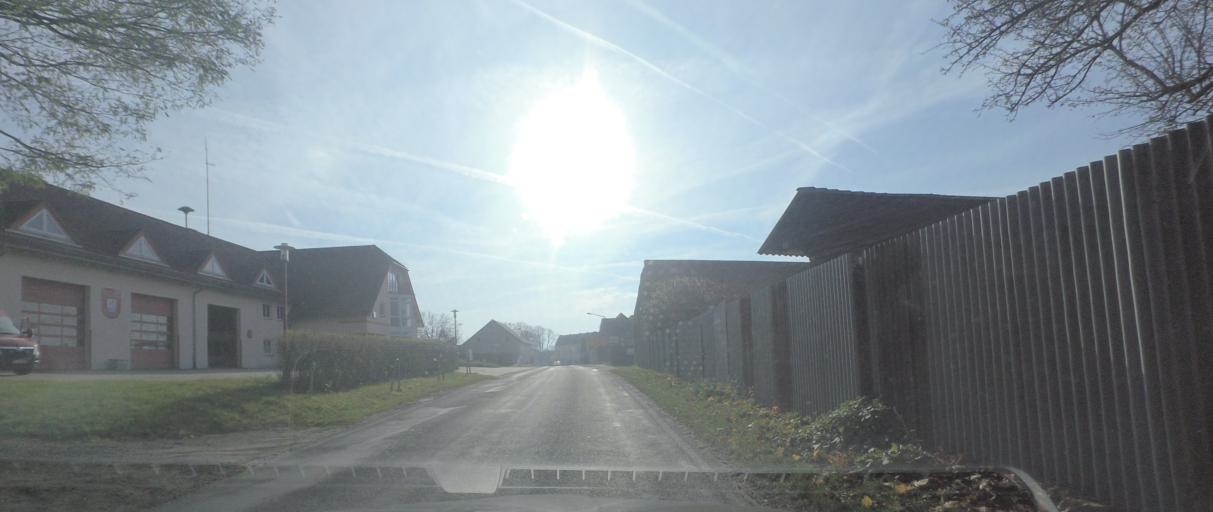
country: DE
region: Brandenburg
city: Sperenberg
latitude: 52.1434
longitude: 13.3656
